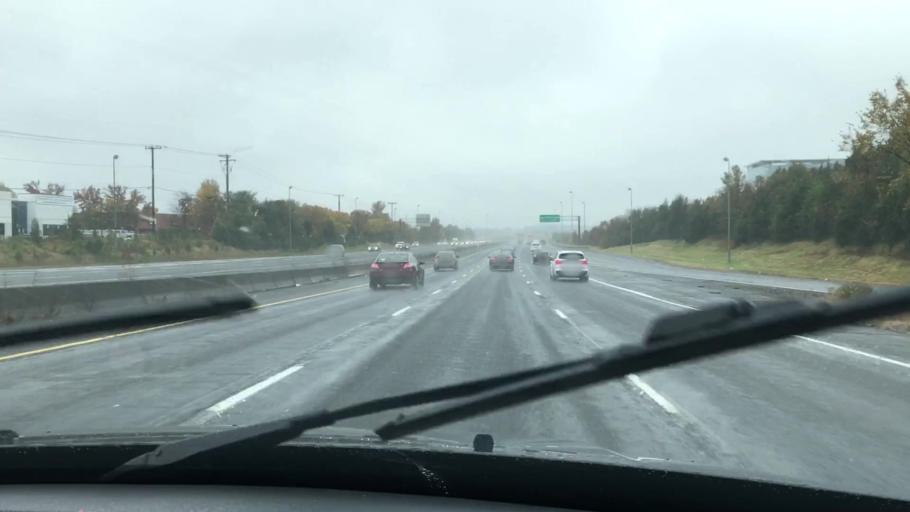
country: US
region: Virginia
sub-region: Fairfax County
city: Chantilly
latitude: 38.8941
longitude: -77.4417
